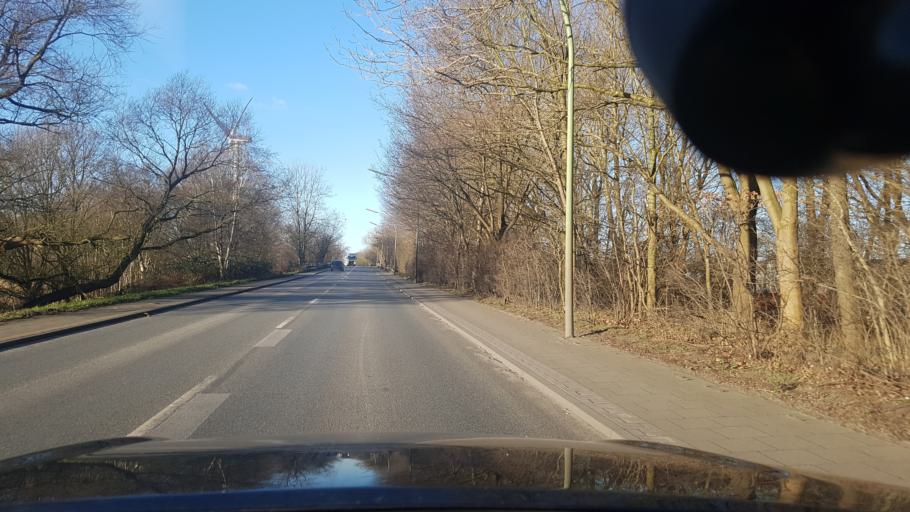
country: DE
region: Lower Saxony
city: Langen
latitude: 53.5903
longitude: 8.5564
